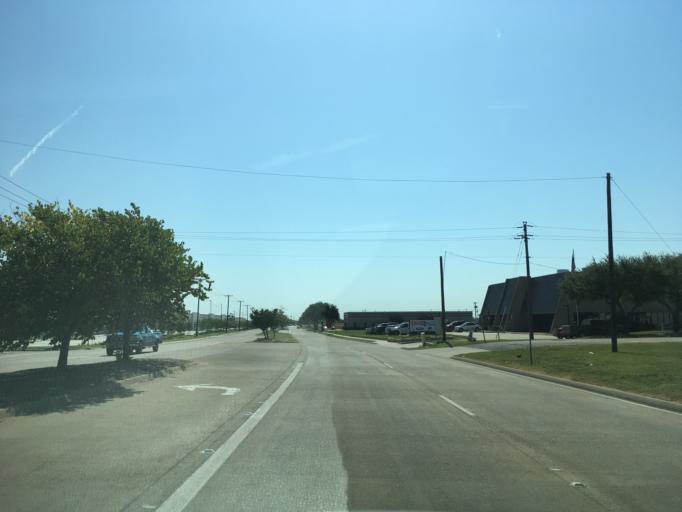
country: US
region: Texas
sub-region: Collin County
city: McKinney
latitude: 33.1780
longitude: -96.6051
